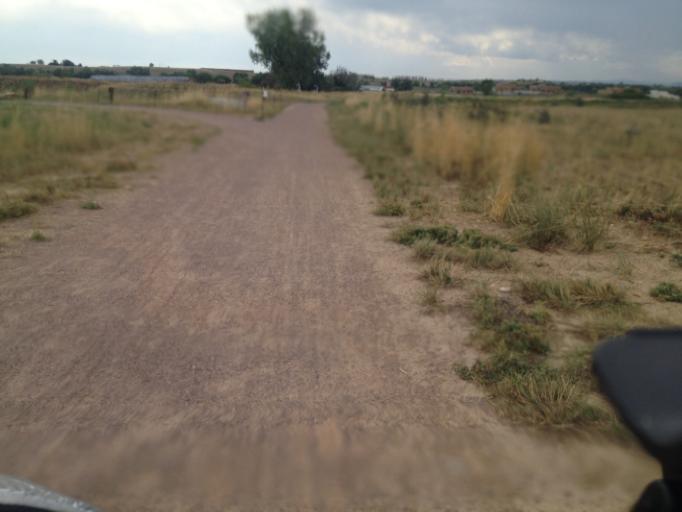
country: US
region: Colorado
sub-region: Boulder County
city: Louisville
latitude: 39.9833
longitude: -105.1188
